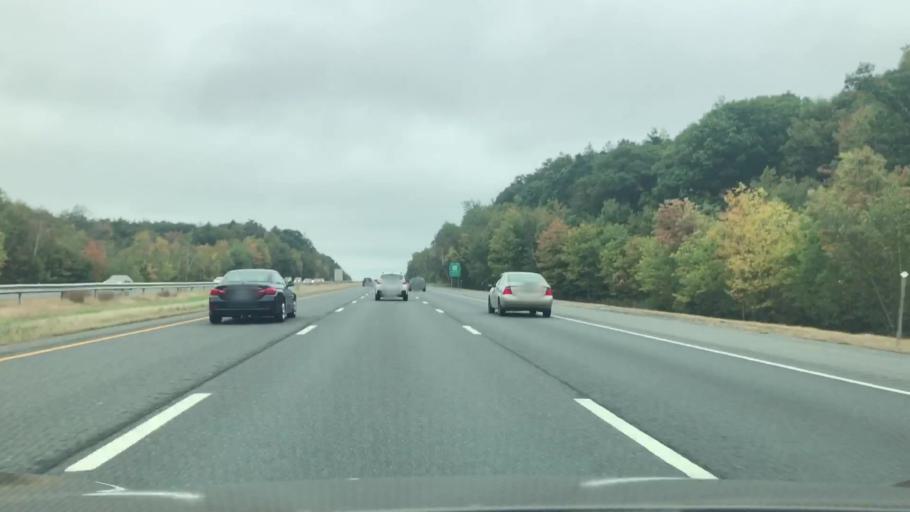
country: US
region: Connecticut
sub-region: Tolland County
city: Stafford
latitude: 41.9653
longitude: -72.1941
